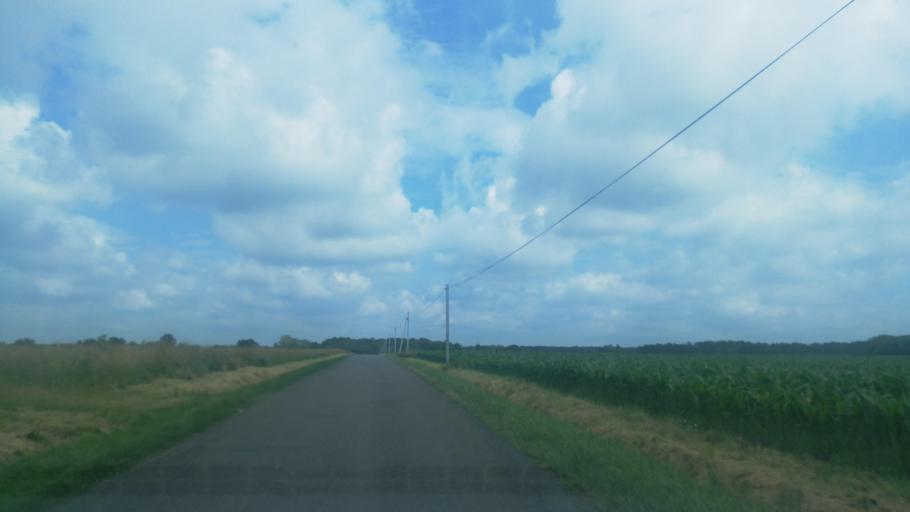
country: FR
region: Centre
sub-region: Departement du Loir-et-Cher
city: Saint-Romain-sur-Cher
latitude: 47.3424
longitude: 1.4491
